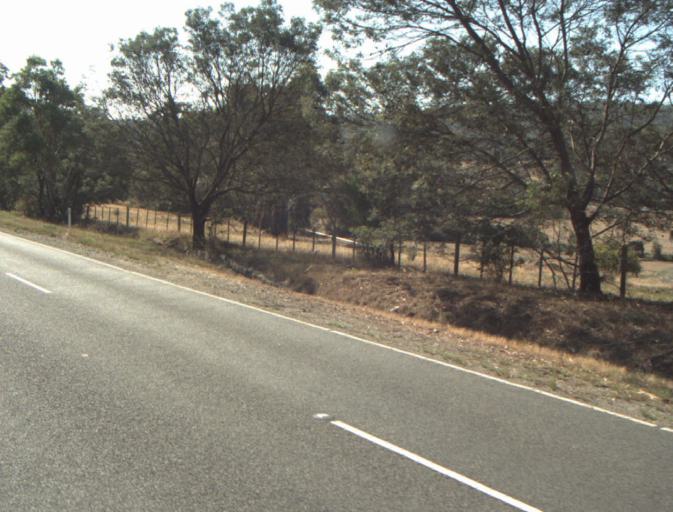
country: AU
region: Tasmania
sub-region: Launceston
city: Mayfield
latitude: -41.3342
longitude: 147.0774
